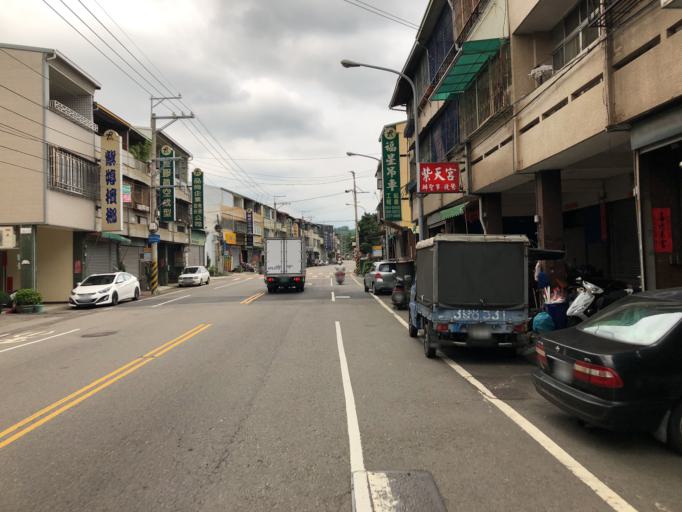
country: TW
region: Taiwan
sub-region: Taichung City
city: Taichung
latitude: 24.1249
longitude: 120.7348
